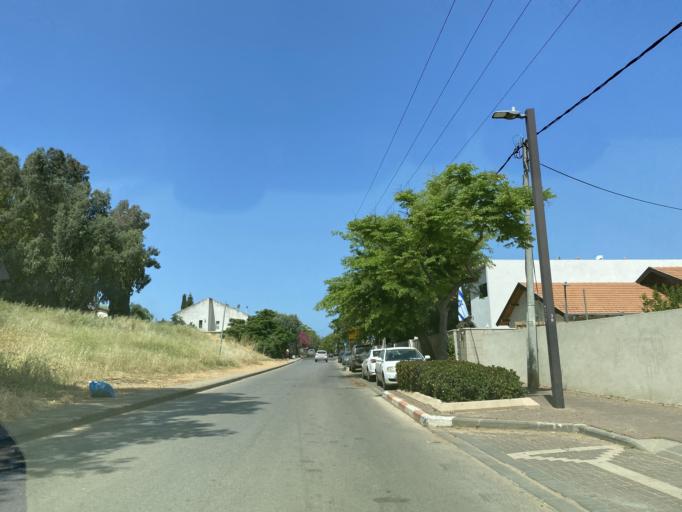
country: IL
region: Tel Aviv
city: Ramat HaSharon
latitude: 32.1534
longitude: 34.8373
